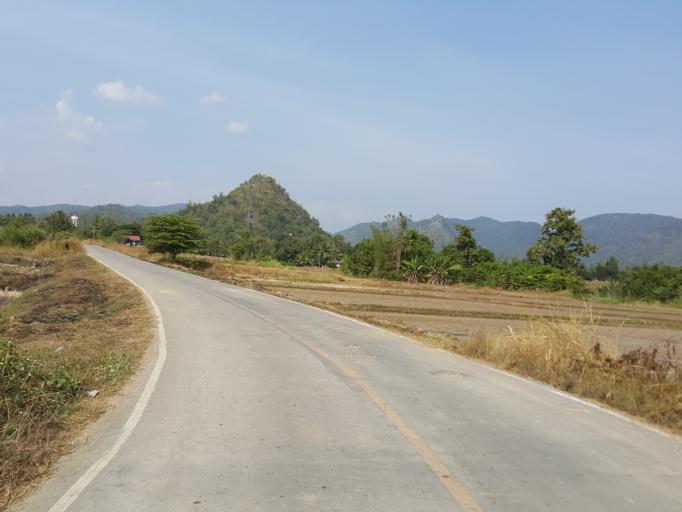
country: TH
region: Sukhothai
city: Thung Saliam
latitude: 17.3400
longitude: 99.4406
